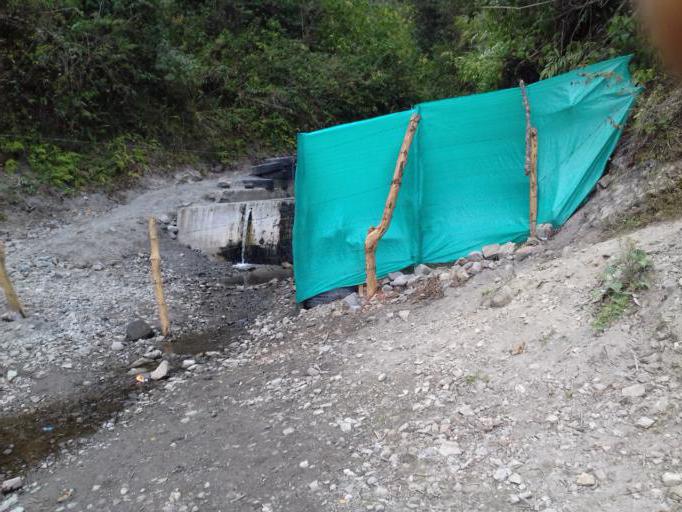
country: CO
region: Tolima
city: Cajamarca
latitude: 4.4748
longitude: -75.3883
